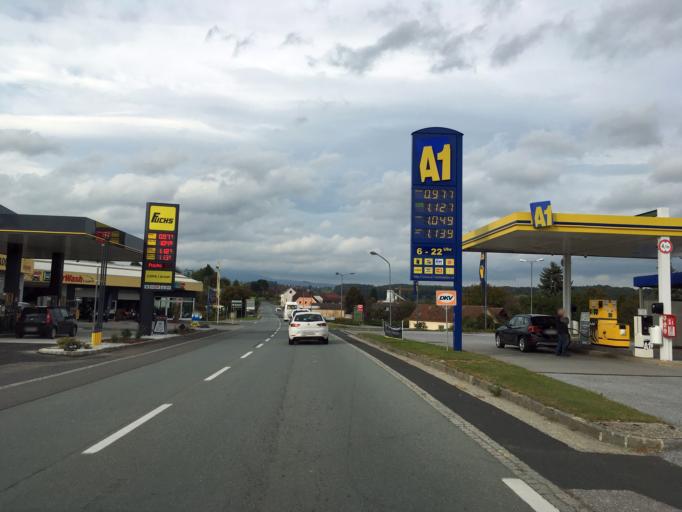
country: AT
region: Styria
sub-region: Politischer Bezirk Hartberg-Fuerstenfeld
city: Grafendorf bei Hartberg
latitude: 47.3276
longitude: 15.9910
